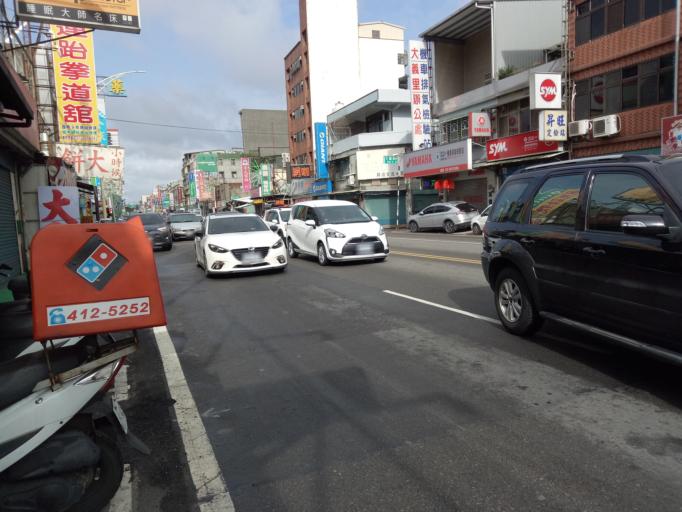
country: TW
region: Taiwan
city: Taoyuan City
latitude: 24.9654
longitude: 121.3007
